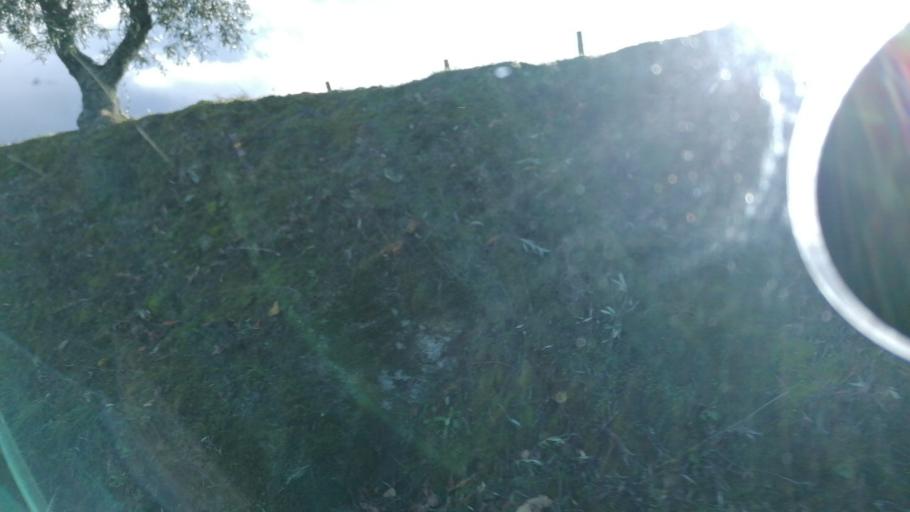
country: PT
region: Vila Real
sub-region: Peso da Regua
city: Peso da Regua
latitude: 41.1290
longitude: -7.7859
